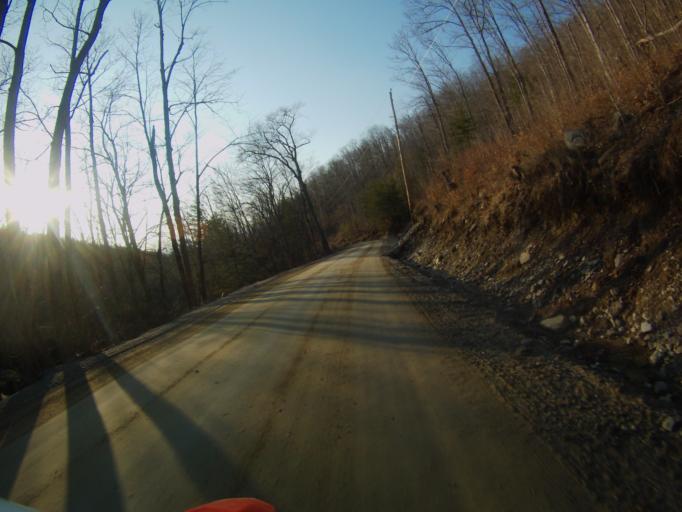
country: US
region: Vermont
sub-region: Addison County
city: Bristol
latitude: 44.0790
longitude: -73.0658
